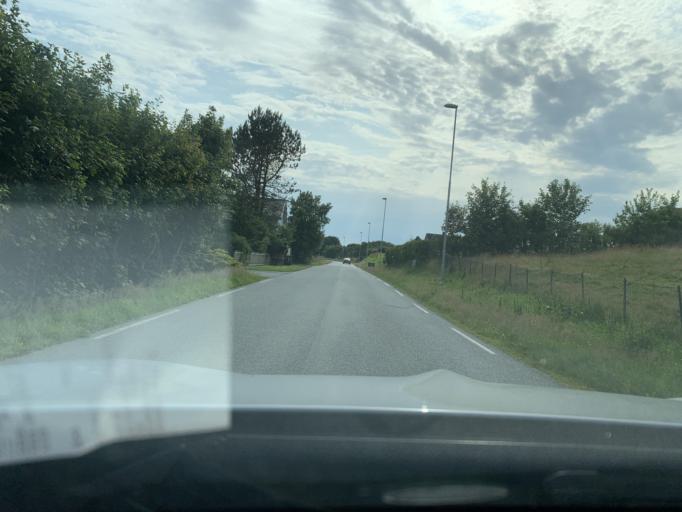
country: NO
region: Rogaland
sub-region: Time
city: Bryne
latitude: 58.7359
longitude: 5.6040
